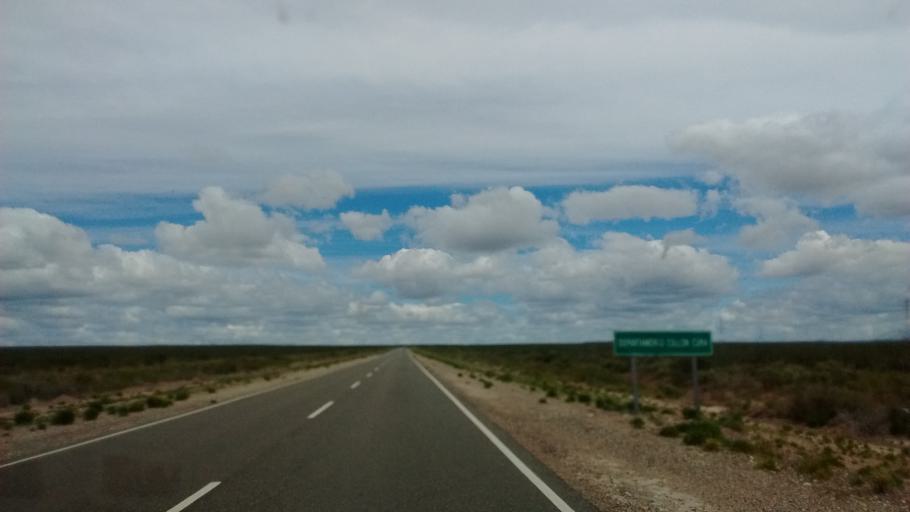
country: AR
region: Neuquen
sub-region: Departamento de Picun Leufu
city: Picun Leufu
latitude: -39.7433
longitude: -69.6072
